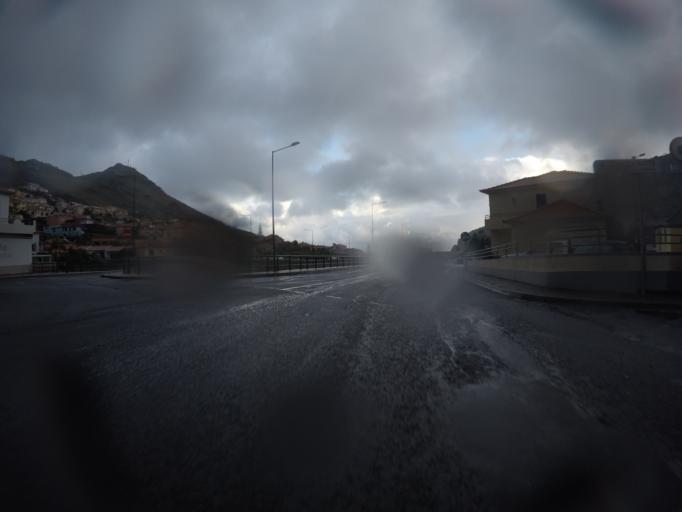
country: PT
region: Madeira
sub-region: Machico
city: Machico
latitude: 32.7239
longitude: -16.7704
